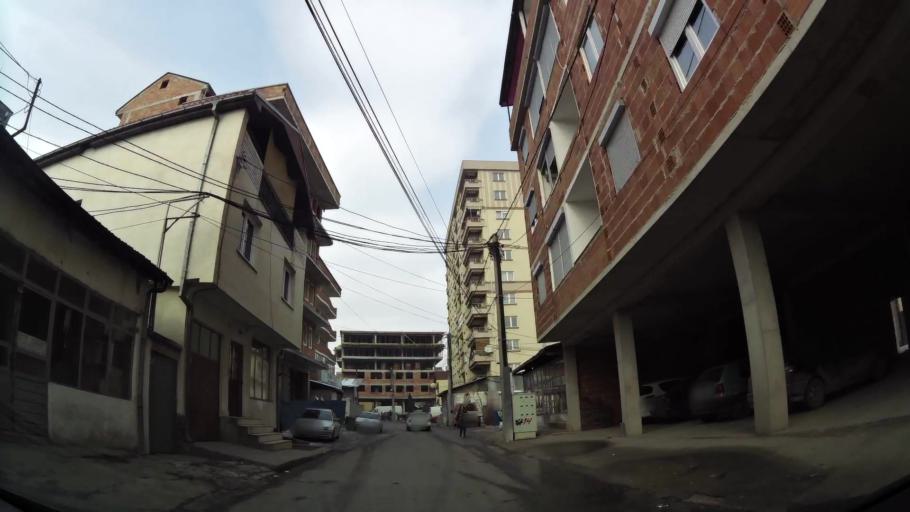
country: MK
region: Cair
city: Cair
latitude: 42.0098
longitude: 21.4347
